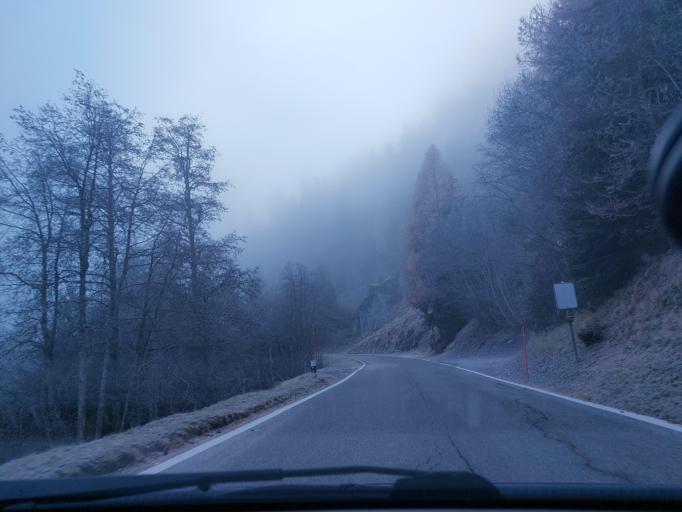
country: CH
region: Valais
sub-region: Conthey District
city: Basse-Nendaz
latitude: 46.1478
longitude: 7.3152
